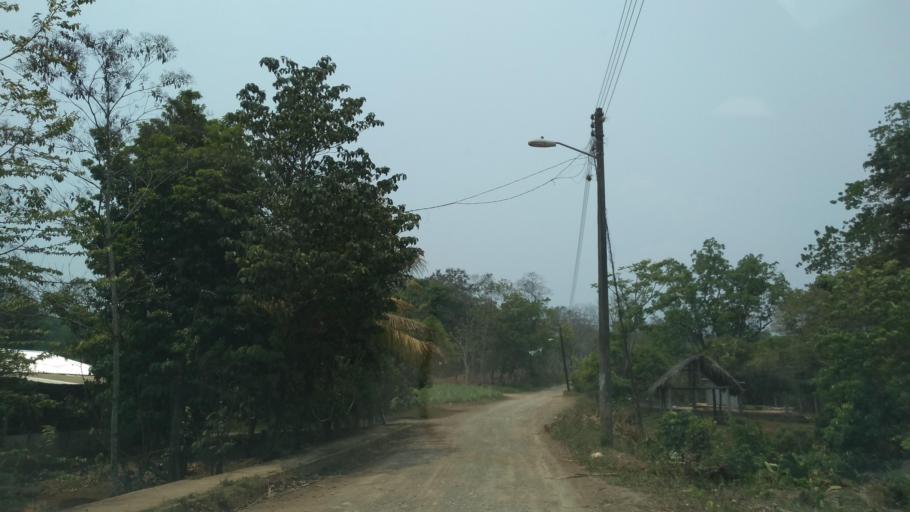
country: MX
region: Puebla
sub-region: San Sebastian Tlacotepec
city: San Martin Mazateopan
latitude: 18.4917
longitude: -96.7810
